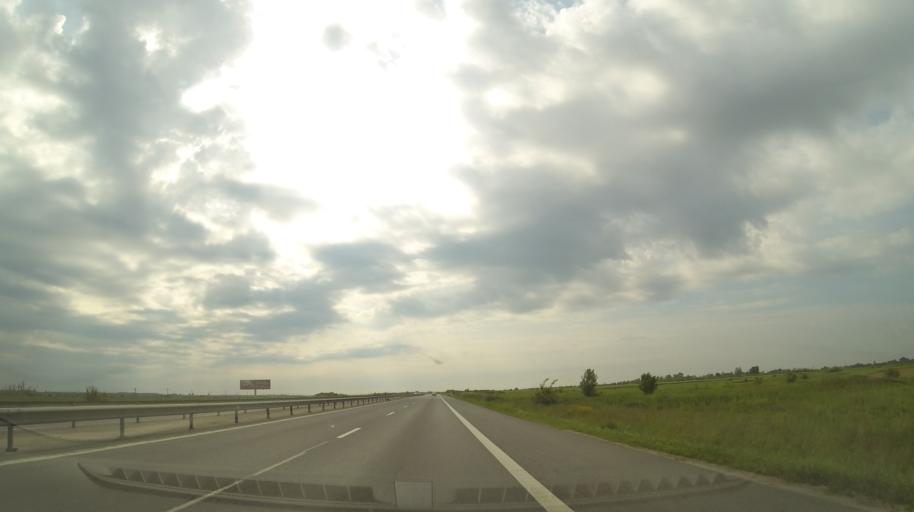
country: RO
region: Dambovita
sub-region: Comuna Mogosani
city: Zavoiu
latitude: 44.6378
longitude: 25.4034
